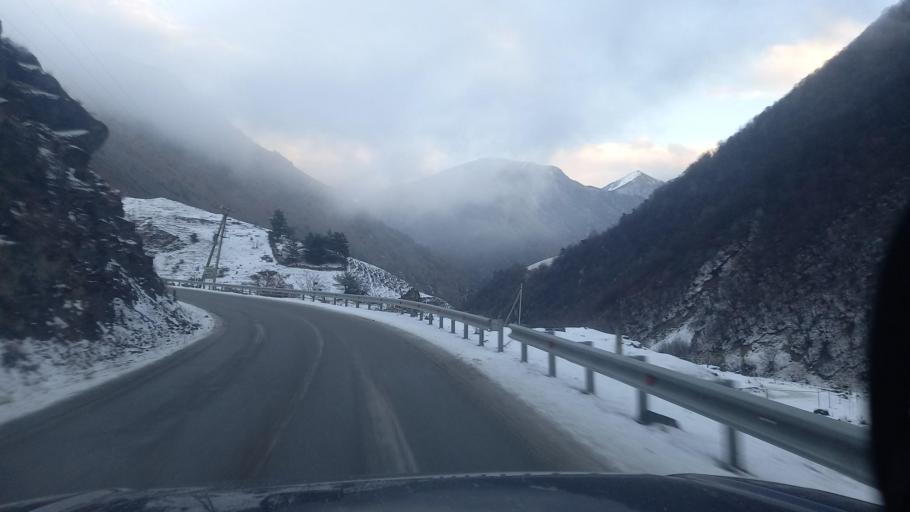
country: RU
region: Ingushetiya
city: Dzhayrakh
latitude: 42.7901
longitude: 44.7769
